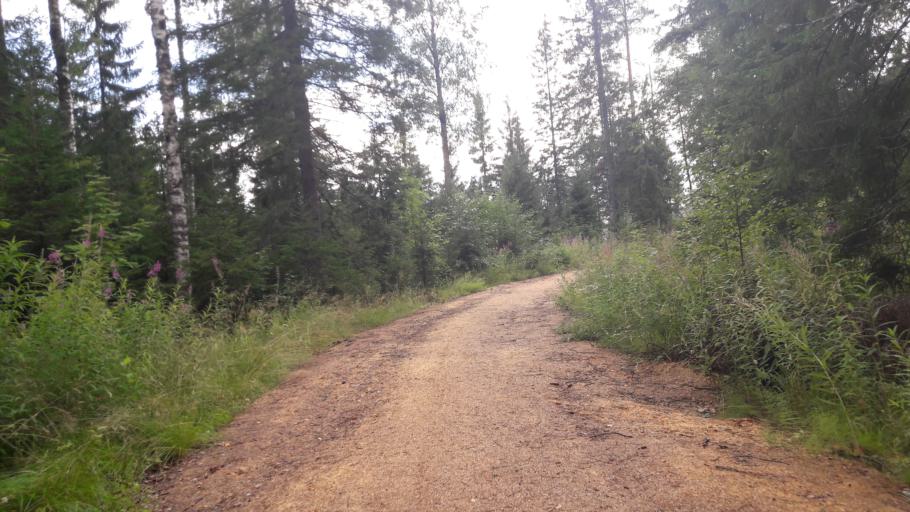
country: FI
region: North Karelia
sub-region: Joensuu
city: Joensuu
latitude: 62.5746
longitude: 29.8274
